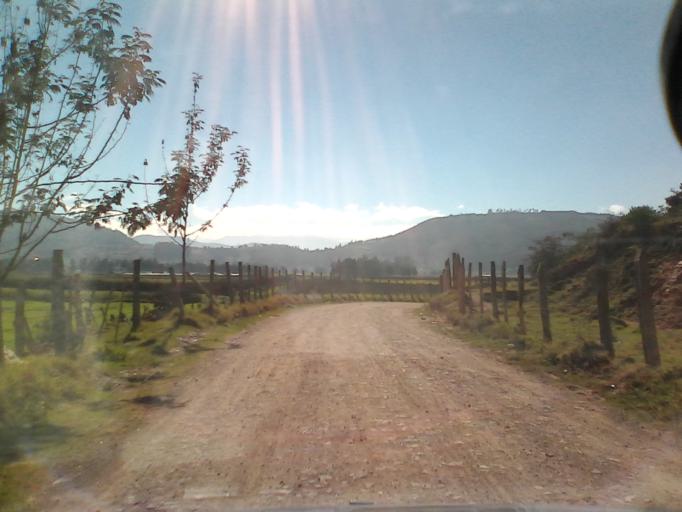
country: CO
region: Boyaca
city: Duitama
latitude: 5.7937
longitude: -73.0370
